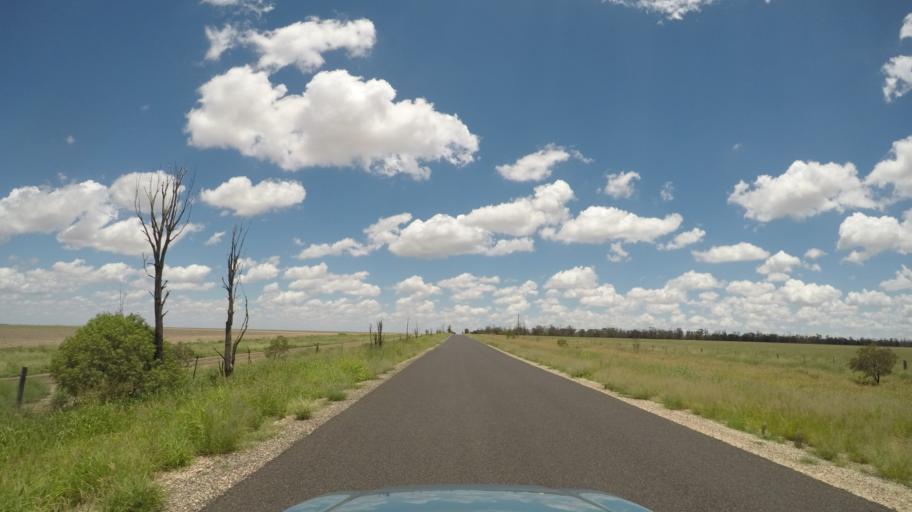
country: AU
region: Queensland
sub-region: Goondiwindi
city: Goondiwindi
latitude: -28.1641
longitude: 150.1621
